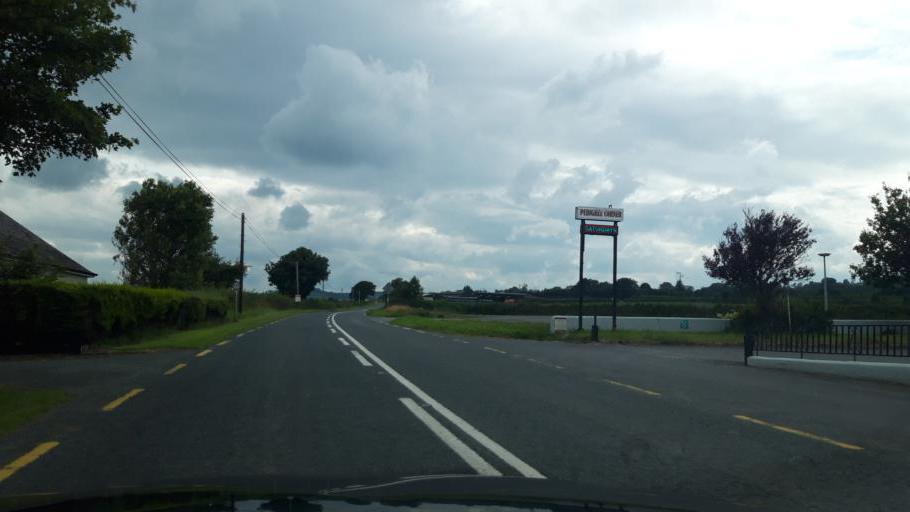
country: IE
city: Ballylinan
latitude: 52.9228
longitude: -7.0621
